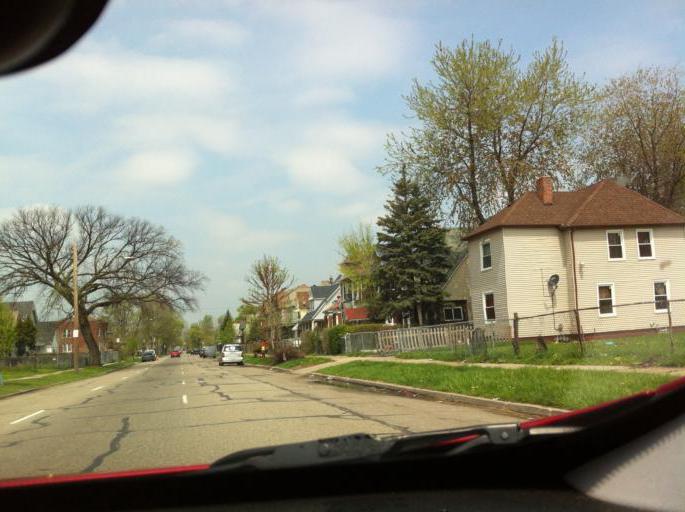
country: US
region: Michigan
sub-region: Wayne County
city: River Rouge
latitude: 42.3094
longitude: -83.1039
